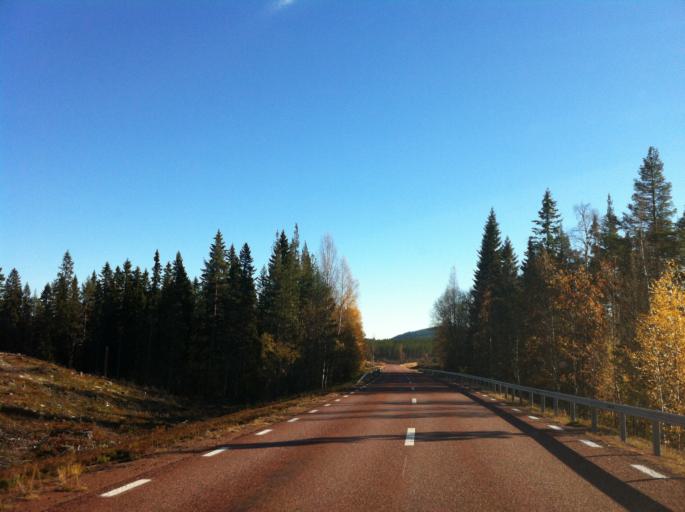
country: SE
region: Dalarna
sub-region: Alvdalens Kommun
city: AElvdalen
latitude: 61.3290
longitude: 13.6009
